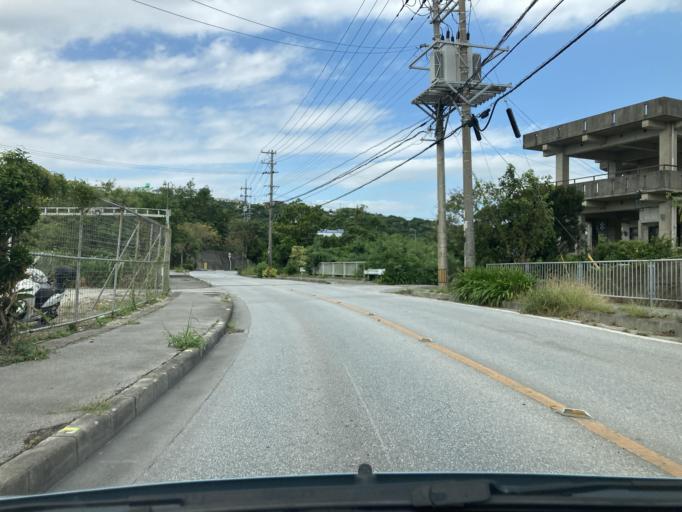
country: JP
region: Okinawa
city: Ginowan
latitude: 26.2735
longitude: 127.7813
